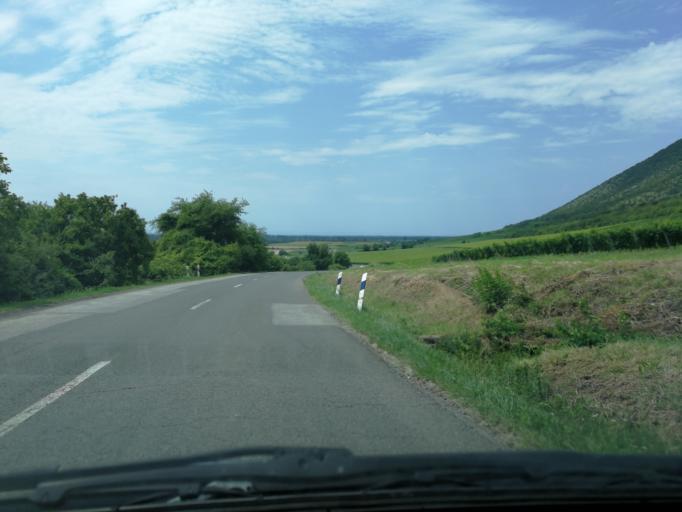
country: HU
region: Baranya
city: Villany
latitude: 45.8542
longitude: 18.4323
